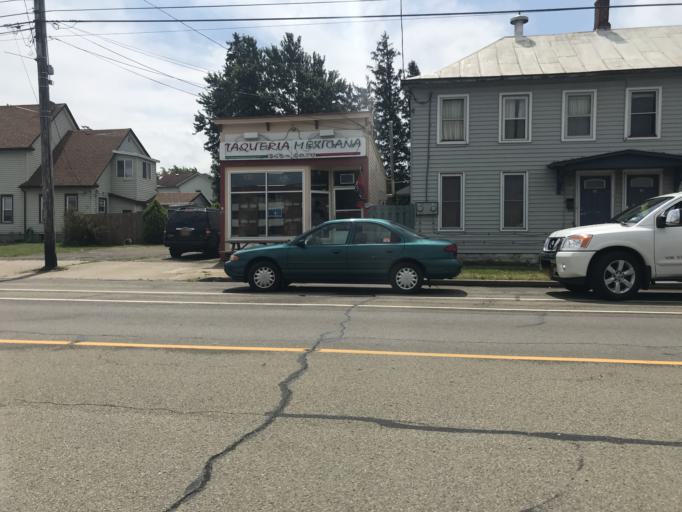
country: US
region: New York
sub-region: Chautauqua County
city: Dunkirk
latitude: 42.4877
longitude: -79.3331
